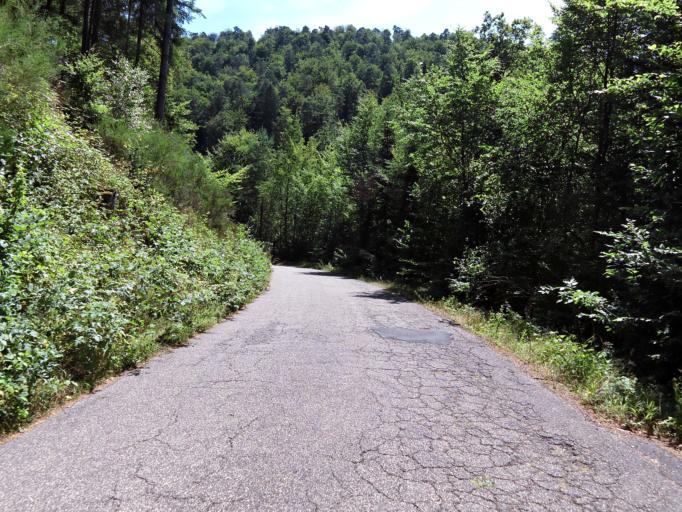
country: DE
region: Rheinland-Pfalz
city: Wilgartswiesen
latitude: 49.2453
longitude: 7.8826
